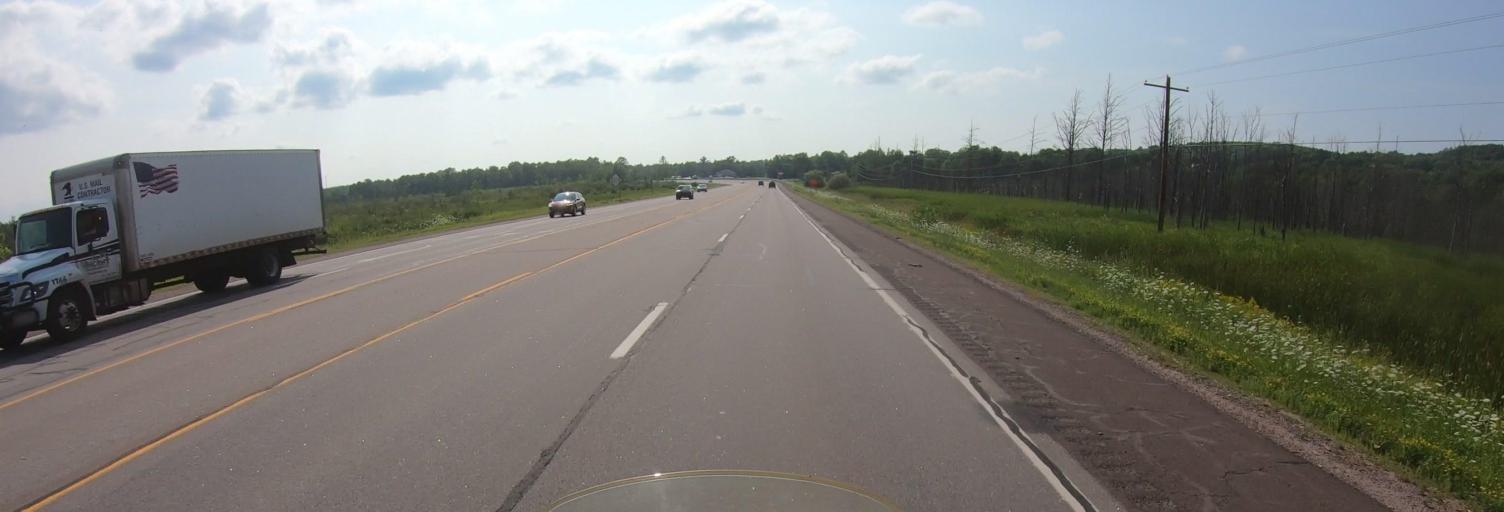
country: US
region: Michigan
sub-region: Gogebic County
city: Bessemer
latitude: 46.4778
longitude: -90.0989
